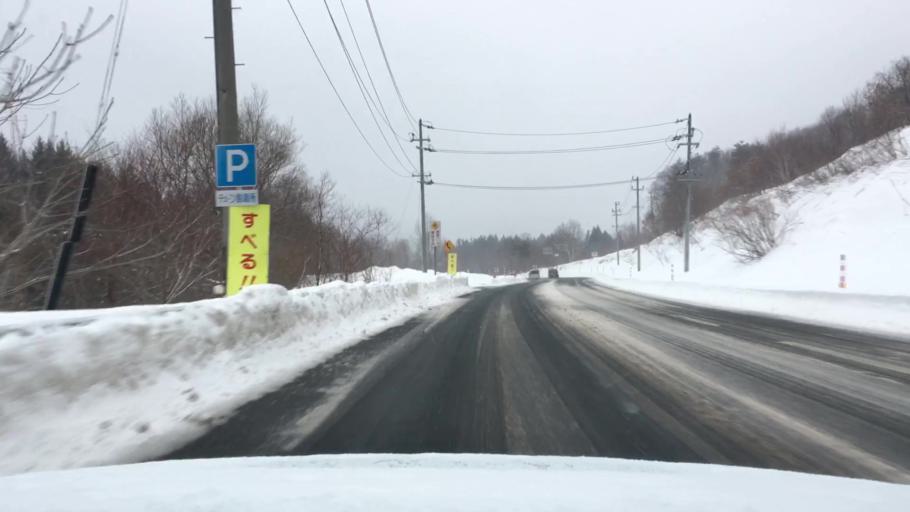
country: JP
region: Akita
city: Hanawa
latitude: 40.0295
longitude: 140.9859
